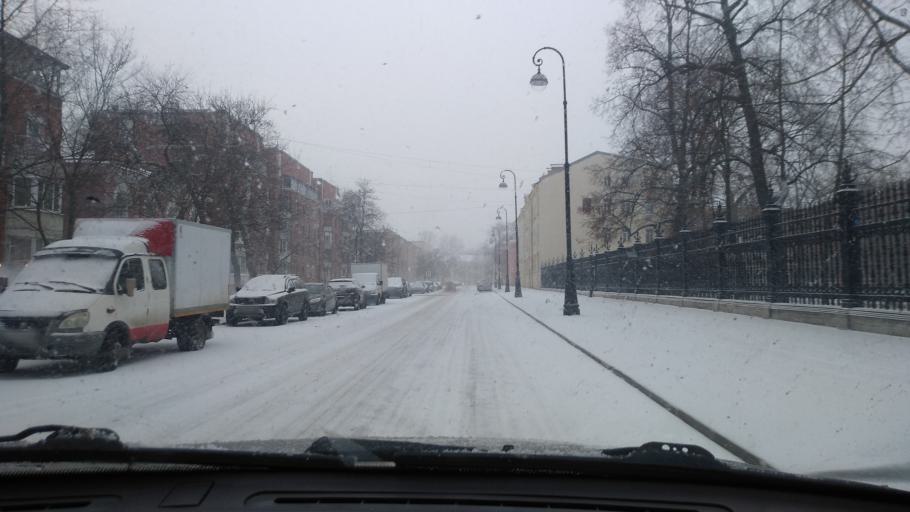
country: RU
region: St.-Petersburg
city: Kronshtadt
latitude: 59.9876
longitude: 29.7760
